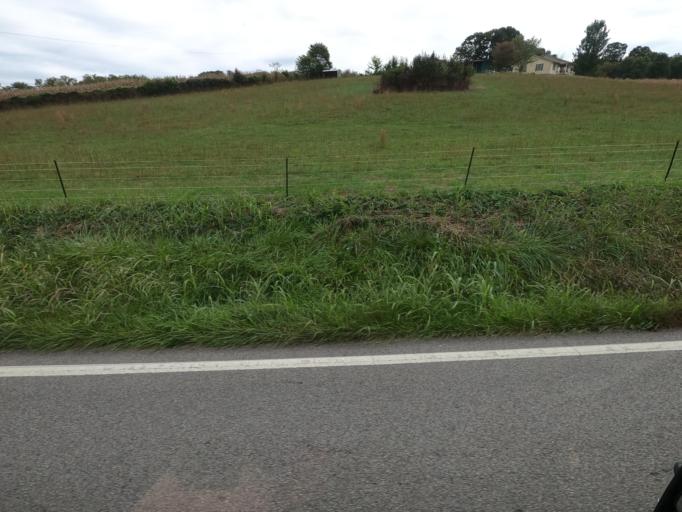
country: US
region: Tennessee
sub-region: Washington County
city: Jonesborough
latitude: 36.2433
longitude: -82.5567
